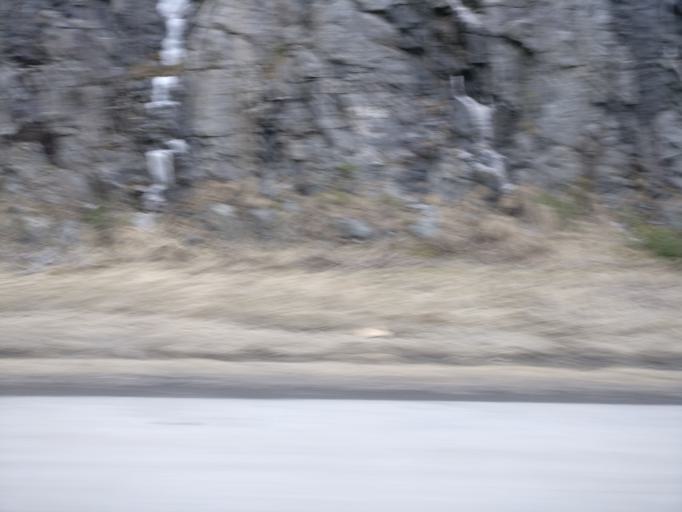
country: FI
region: Pirkanmaa
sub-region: Etelae-Pirkanmaa
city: Akaa
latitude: 61.1782
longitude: 23.9052
